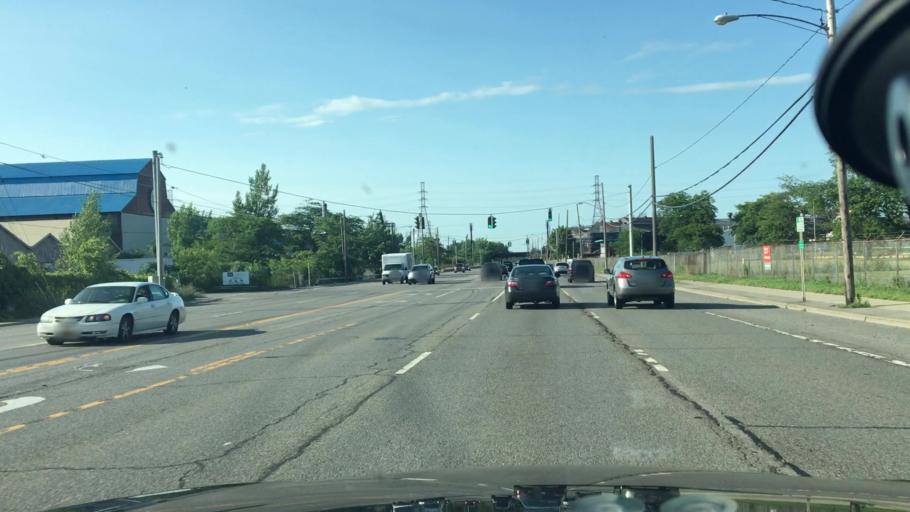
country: US
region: New York
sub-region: Erie County
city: Blasdell
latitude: 42.7998
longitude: -78.8466
